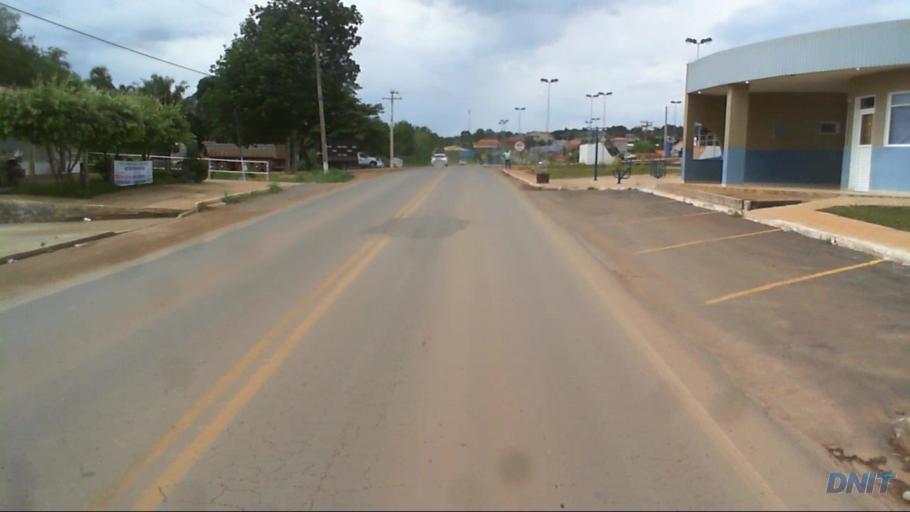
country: BR
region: Goias
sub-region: Padre Bernardo
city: Padre Bernardo
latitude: -15.1727
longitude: -48.2857
